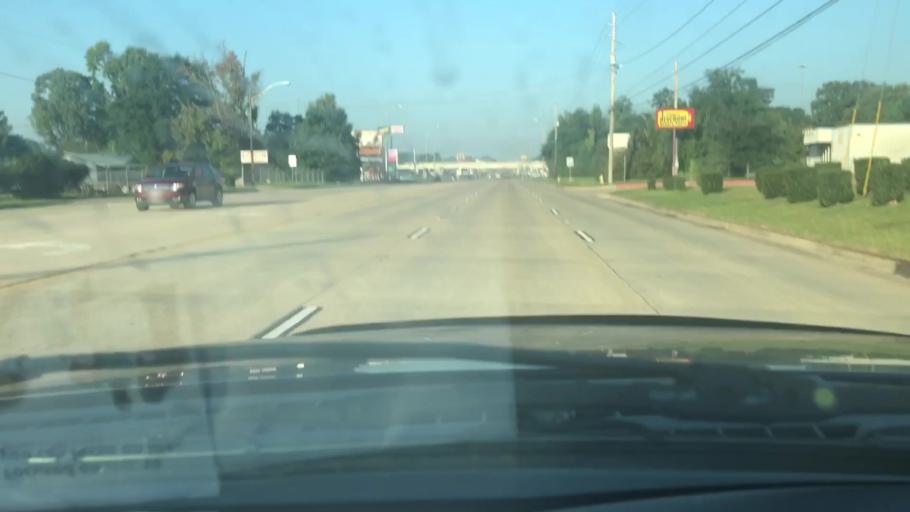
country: US
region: Texas
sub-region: Bowie County
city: Wake Village
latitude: 33.4194
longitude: -94.0918
